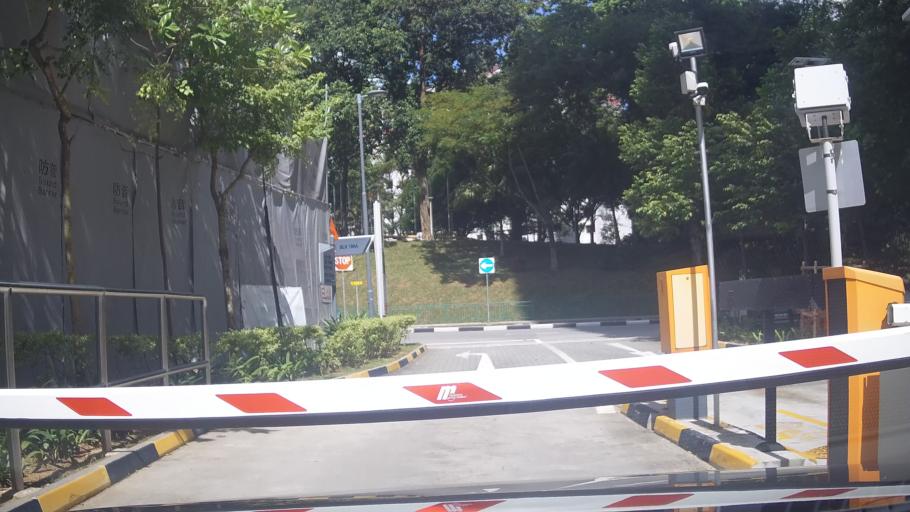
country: MY
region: Johor
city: Johor Bahru
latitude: 1.4391
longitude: 103.7780
